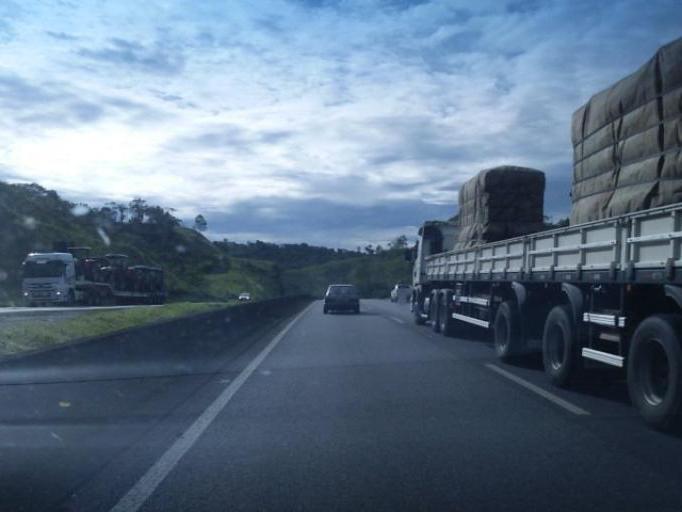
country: BR
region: Parana
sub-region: Antonina
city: Antonina
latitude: -25.1017
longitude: -48.7257
